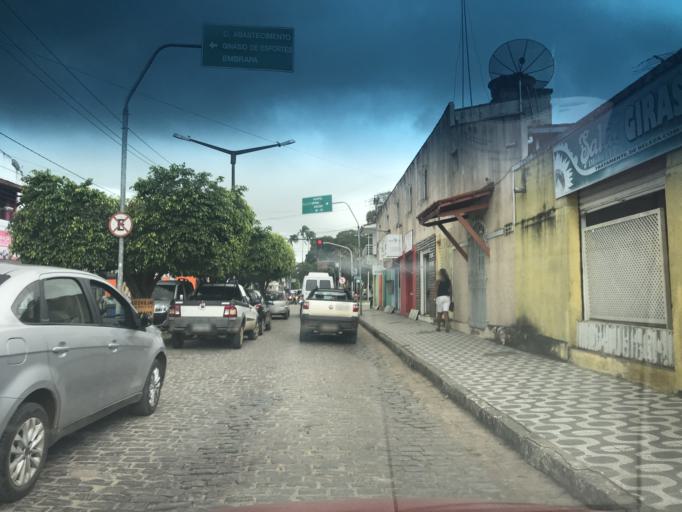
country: BR
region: Bahia
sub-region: Cruz Das Almas
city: Cruz das Almas
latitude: -12.6736
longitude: -39.0998
